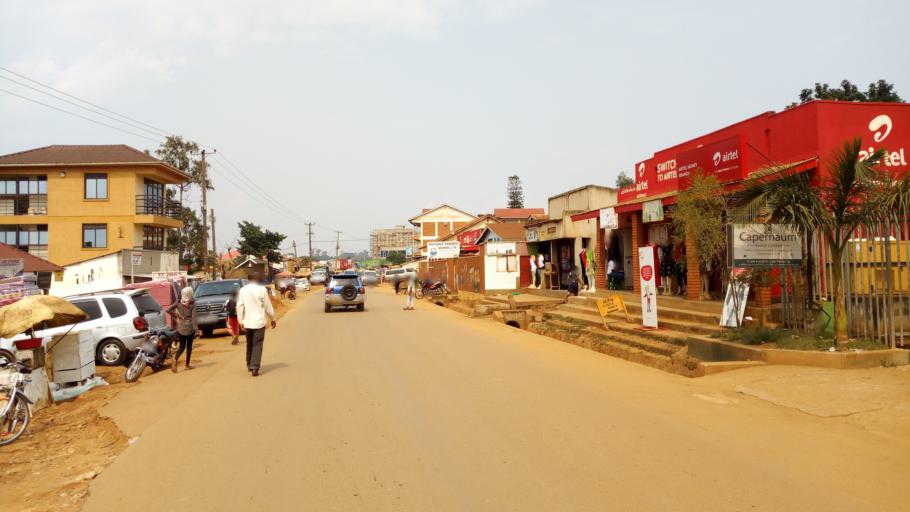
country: UG
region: Central Region
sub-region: Wakiso District
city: Kireka
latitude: 0.3199
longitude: 32.6468
